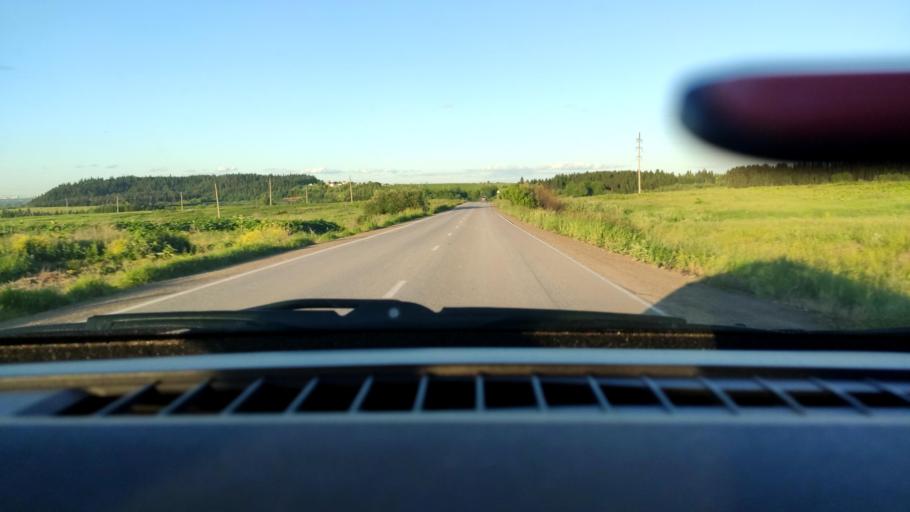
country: RU
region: Perm
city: Kultayevo
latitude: 57.9233
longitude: 55.9120
